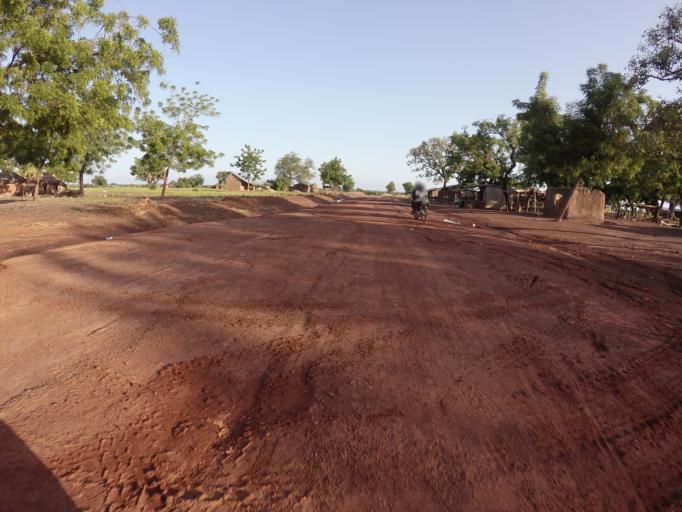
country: TG
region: Savanes
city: Sansanne-Mango
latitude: 10.3553
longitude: -0.0932
